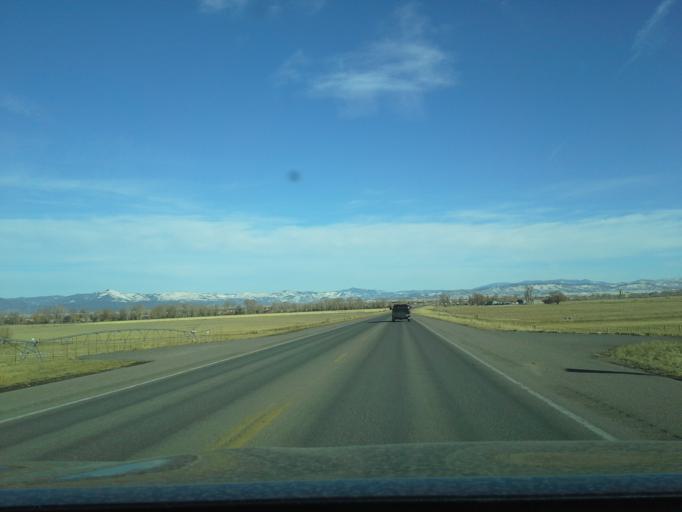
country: US
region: Montana
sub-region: Lewis and Clark County
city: Helena Valley Southeast
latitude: 46.6166
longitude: -111.9761
